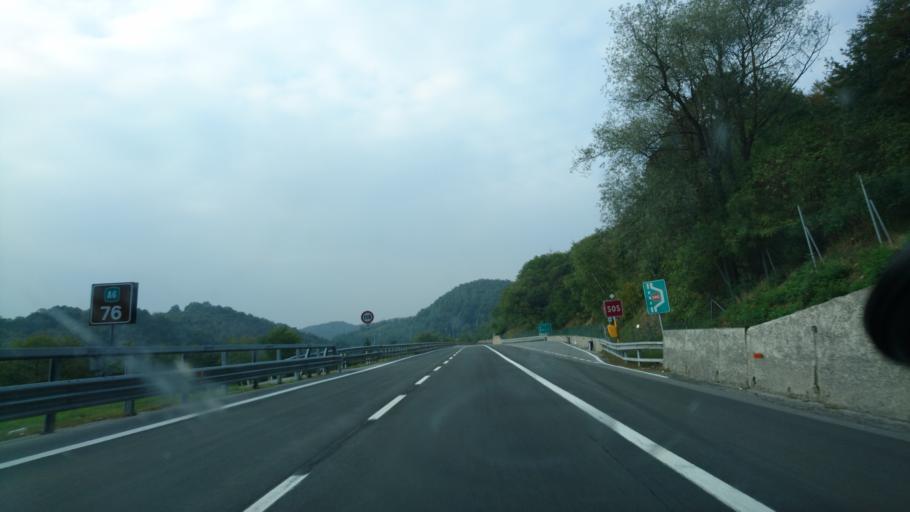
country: IT
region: Liguria
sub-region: Provincia di Savona
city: Altare
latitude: 44.3398
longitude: 8.3289
